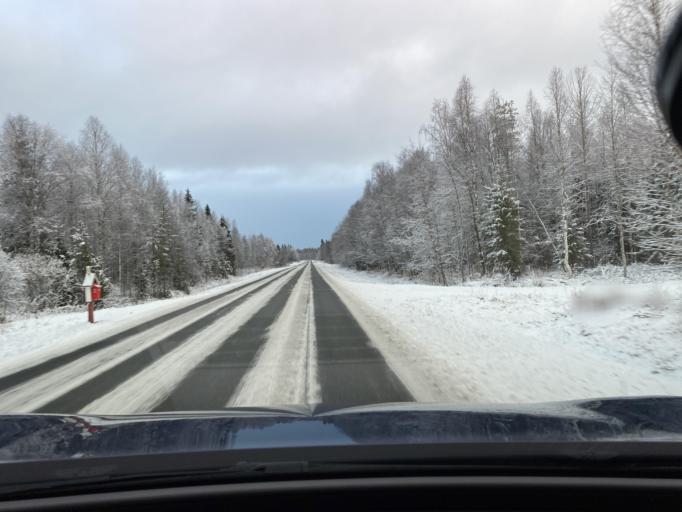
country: FI
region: Lapland
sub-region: Rovaniemi
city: Ranua
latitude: 65.9614
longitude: 26.0485
